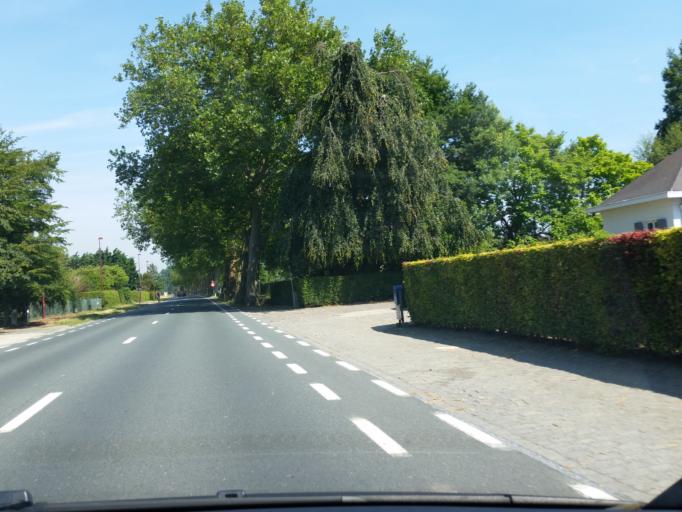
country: BE
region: Flanders
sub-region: Provincie Vlaams-Brabant
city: Steenokkerzeel
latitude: 50.9390
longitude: 4.4946
